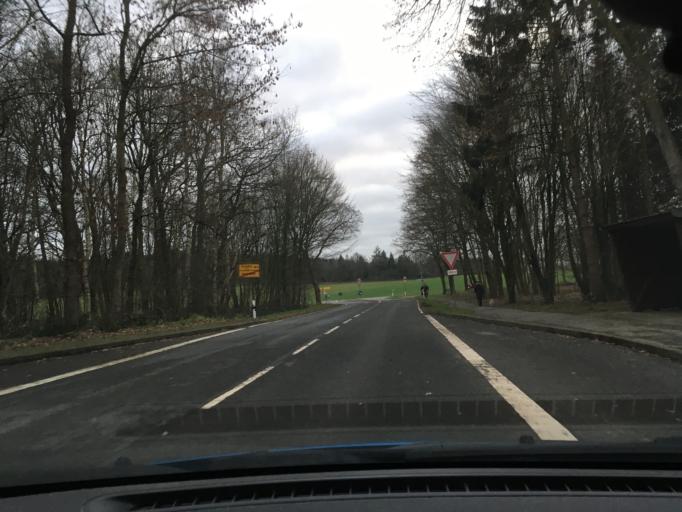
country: DE
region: Schleswig-Holstein
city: Mehlbek
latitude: 53.9974
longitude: 9.4410
